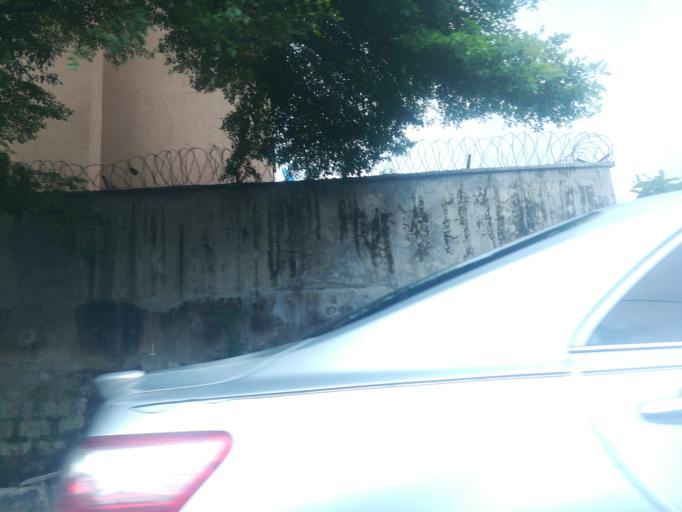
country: NG
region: Lagos
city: Somolu
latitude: 6.5574
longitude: 3.3840
